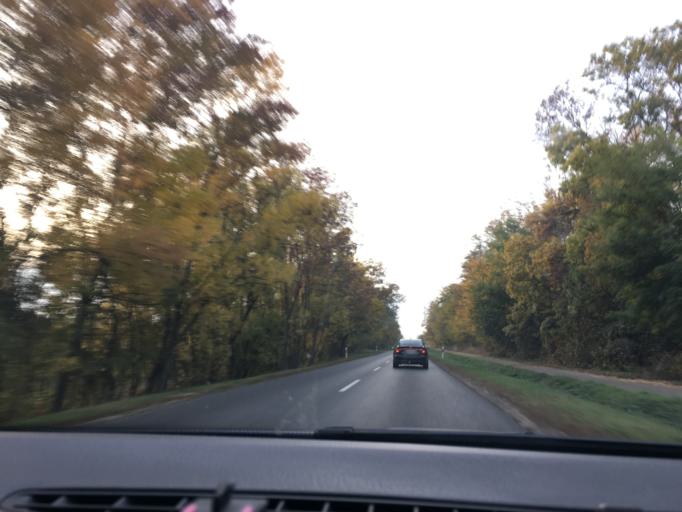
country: HU
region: Szabolcs-Szatmar-Bereg
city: Nagykallo
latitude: 47.8674
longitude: 21.8775
